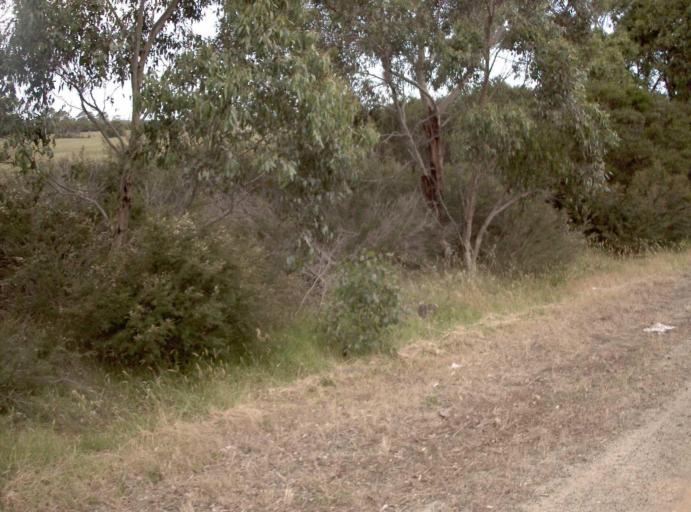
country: AU
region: Victoria
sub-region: Wellington
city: Sale
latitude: -38.2011
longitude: 147.0968
